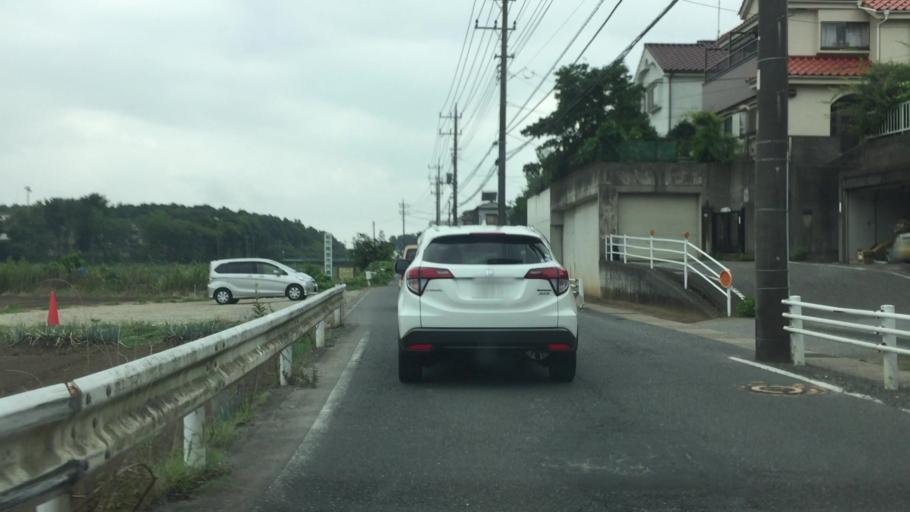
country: JP
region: Chiba
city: Kashiwa
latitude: 35.8237
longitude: 139.9926
